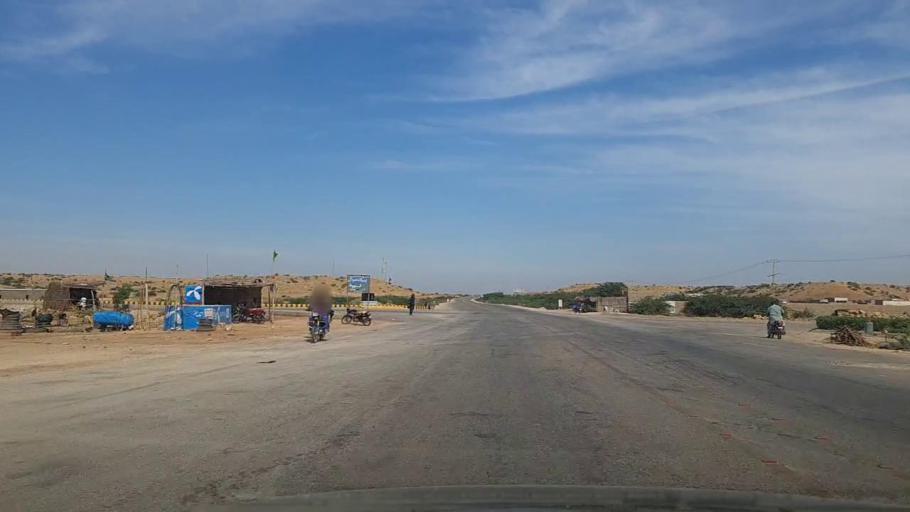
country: PK
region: Sindh
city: Bulri
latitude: 25.0432
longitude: 68.2420
